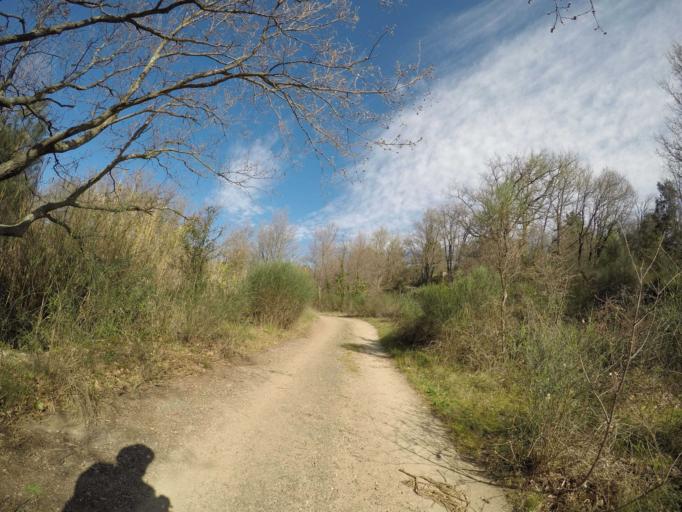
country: FR
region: Languedoc-Roussillon
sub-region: Departement des Pyrenees-Orientales
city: Millas
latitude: 42.7086
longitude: 2.7007
